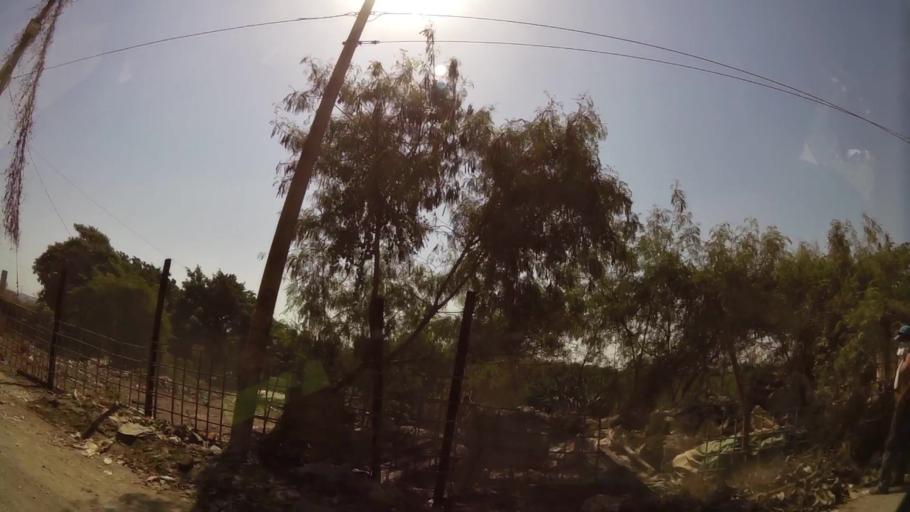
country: CO
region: Bolivar
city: Cartagena
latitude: 10.3582
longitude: -75.4890
